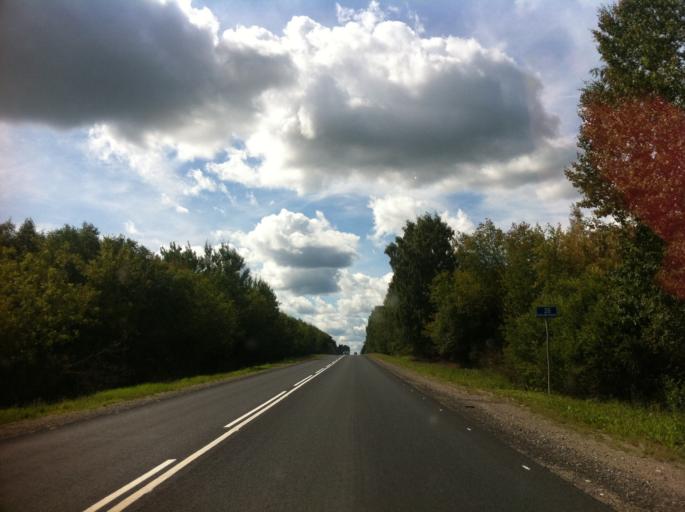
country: RU
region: Pskov
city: Izborsk
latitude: 57.7215
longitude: 27.9379
